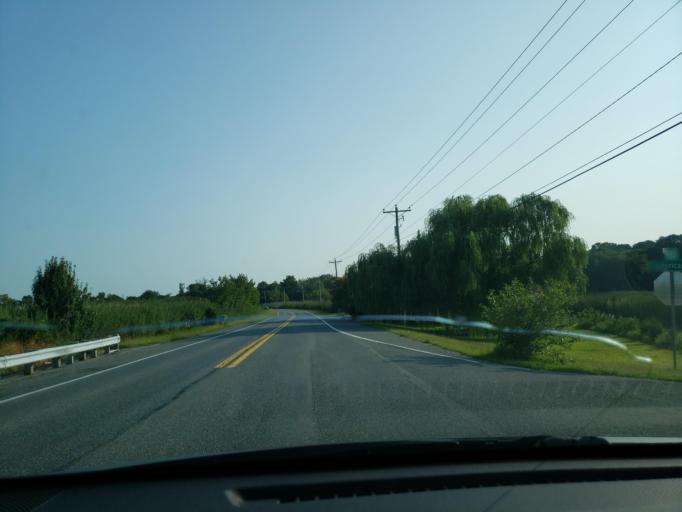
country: US
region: Delaware
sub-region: Kent County
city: Riverview
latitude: 39.0131
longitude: -75.4638
